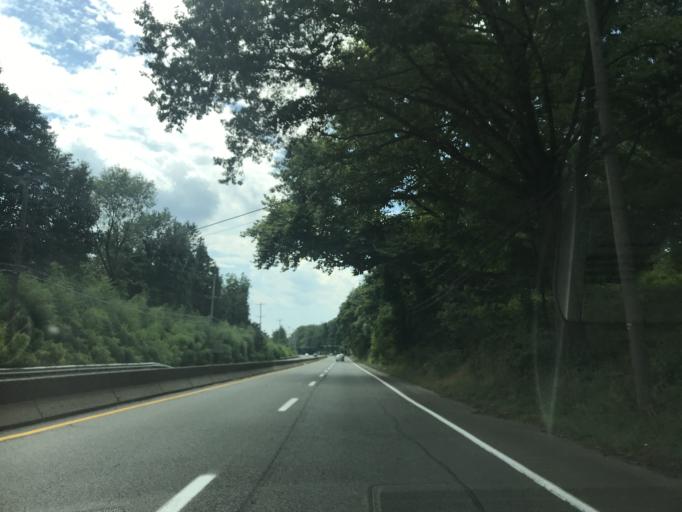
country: US
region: Pennsylvania
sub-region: Chester County
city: West Chester
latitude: 39.8735
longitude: -75.5738
